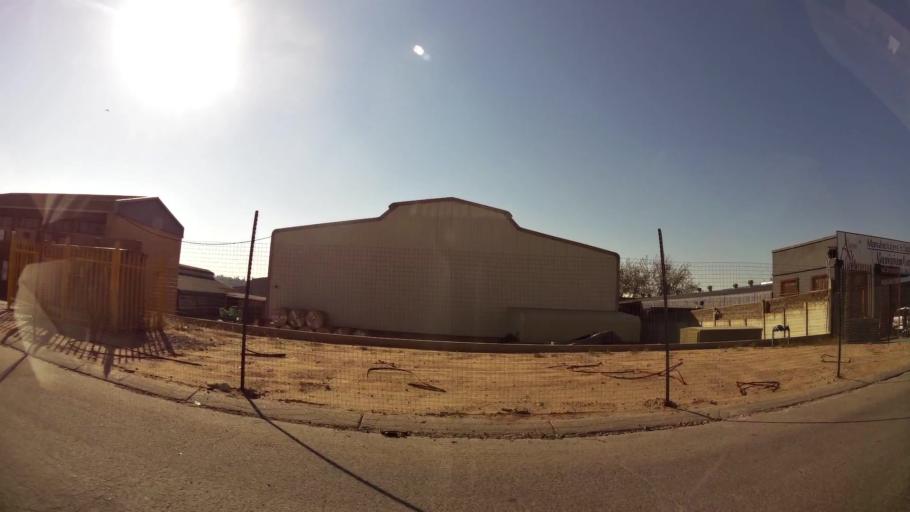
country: ZA
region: Gauteng
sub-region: City of Johannesburg Metropolitan Municipality
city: Modderfontein
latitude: -26.0634
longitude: 28.1945
